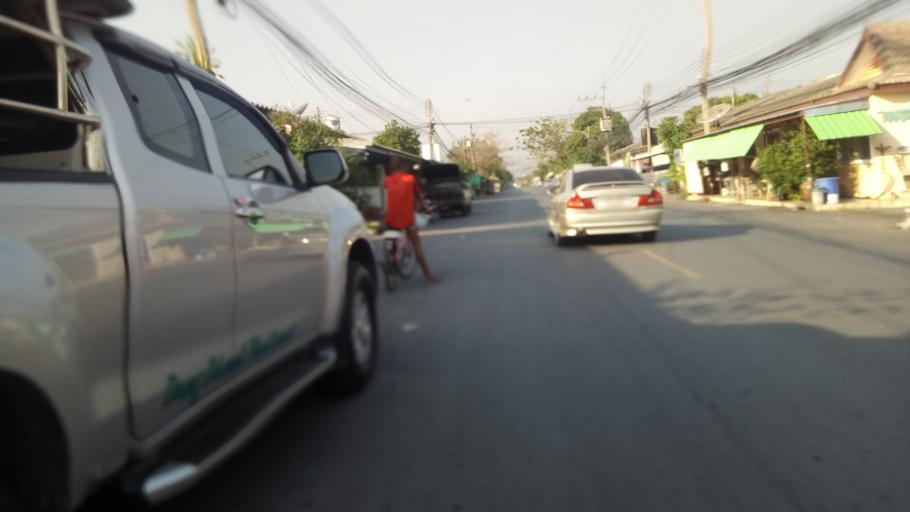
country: TH
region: Pathum Thani
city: Nong Suea
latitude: 14.0539
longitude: 100.8566
